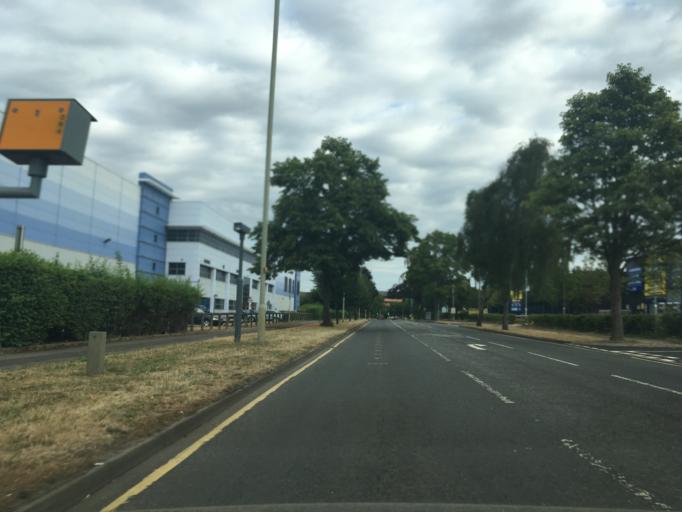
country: GB
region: England
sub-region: Hertfordshire
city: Hemel Hempstead
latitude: 51.7647
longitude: -0.4415
